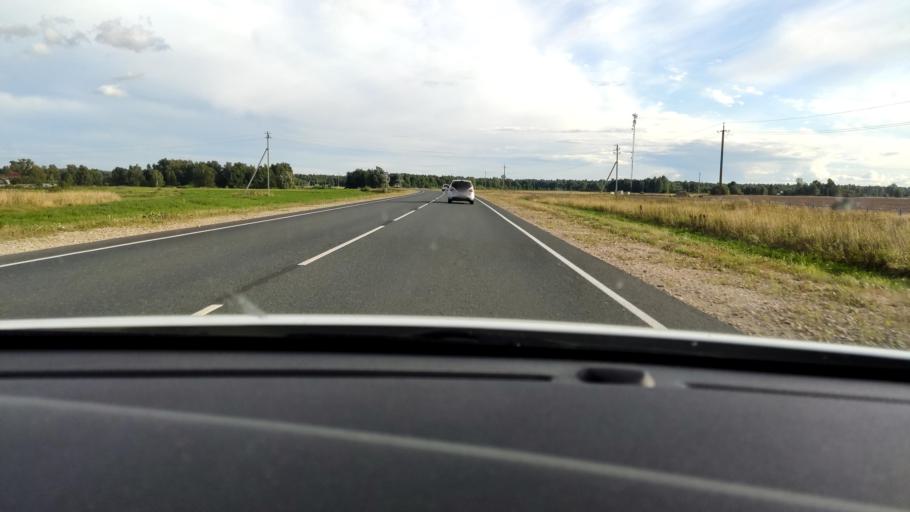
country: RU
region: Mariy-El
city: Krasnogorskiy
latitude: 56.2009
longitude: 48.2355
